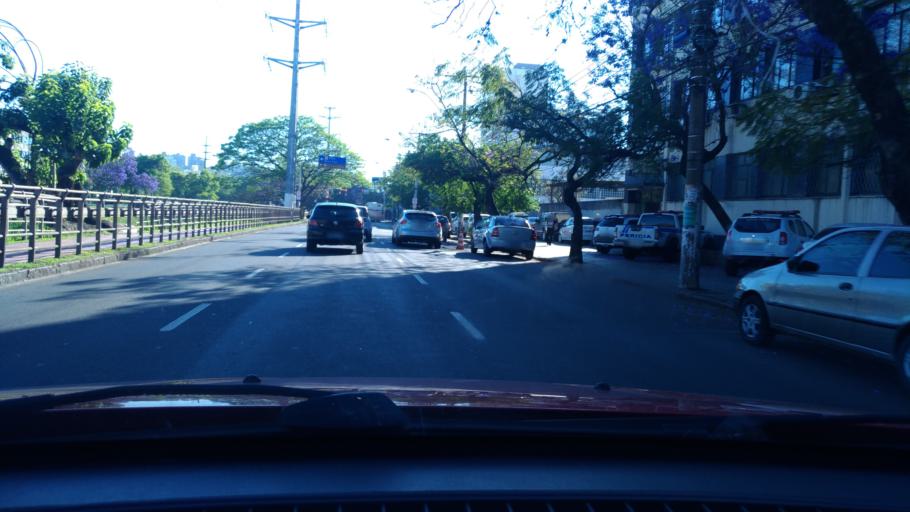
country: BR
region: Rio Grande do Sul
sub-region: Porto Alegre
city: Porto Alegre
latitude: -30.0466
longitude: -51.2109
